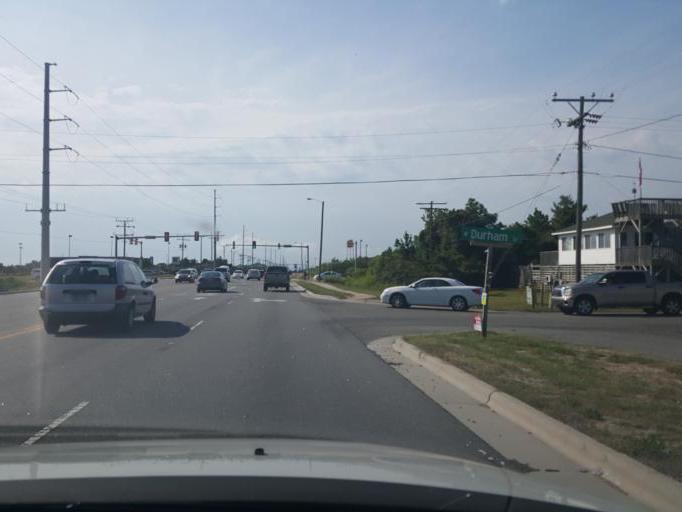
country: US
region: North Carolina
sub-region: Dare County
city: Kill Devil Hills
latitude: 36.0386
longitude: -75.6758
